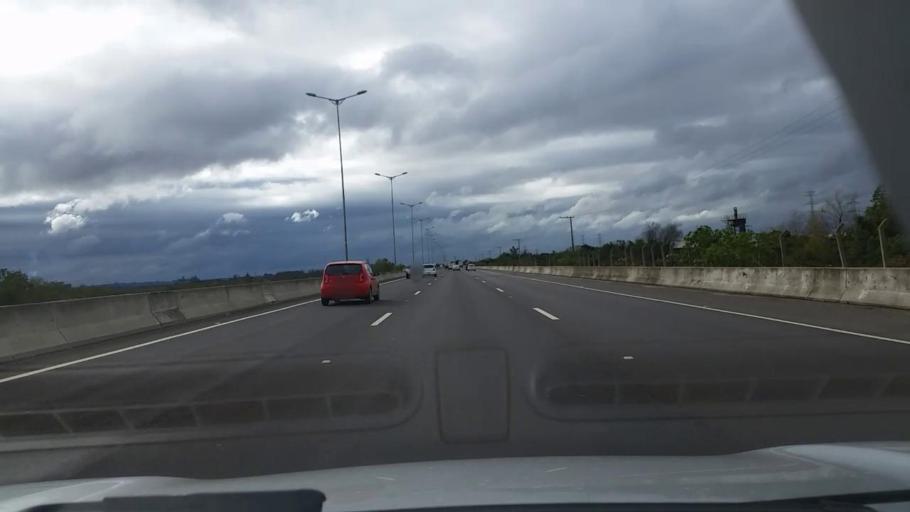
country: BR
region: Rio Grande do Sul
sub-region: Canoas
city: Canoas
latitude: -29.9497
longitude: -51.2035
